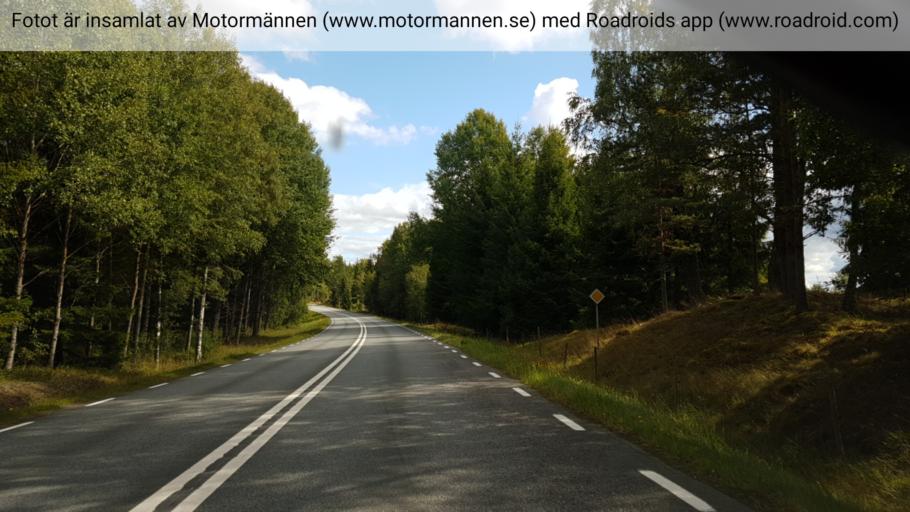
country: SE
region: Joenkoeping
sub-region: Aneby Kommun
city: Hestra
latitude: 57.7716
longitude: 14.5031
